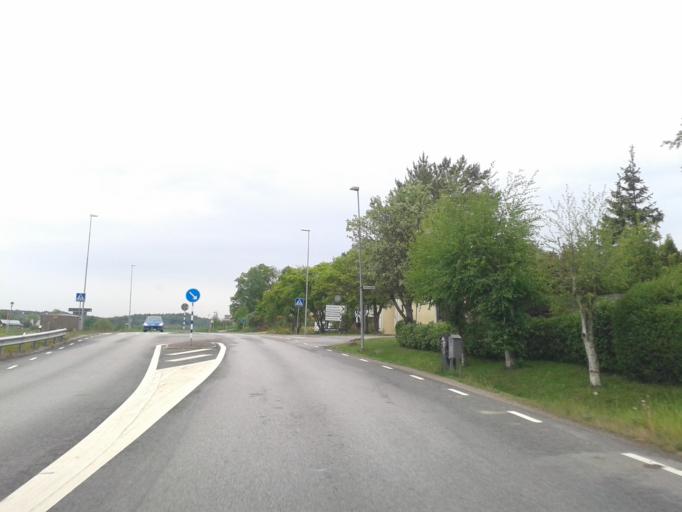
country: SE
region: Vaestra Goetaland
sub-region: Kungalvs Kommun
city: Kode
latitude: 57.8463
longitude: 11.7975
